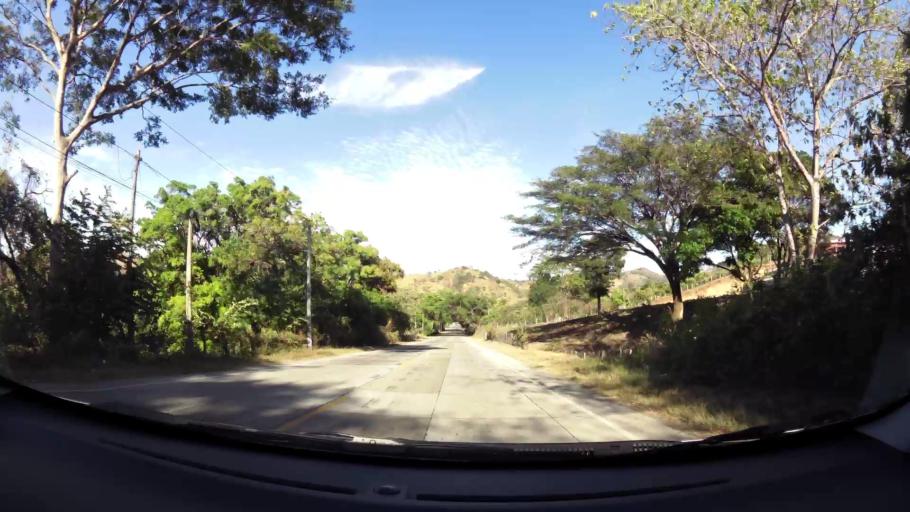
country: SV
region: Santa Ana
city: Texistepeque
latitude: 14.1569
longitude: -89.5062
